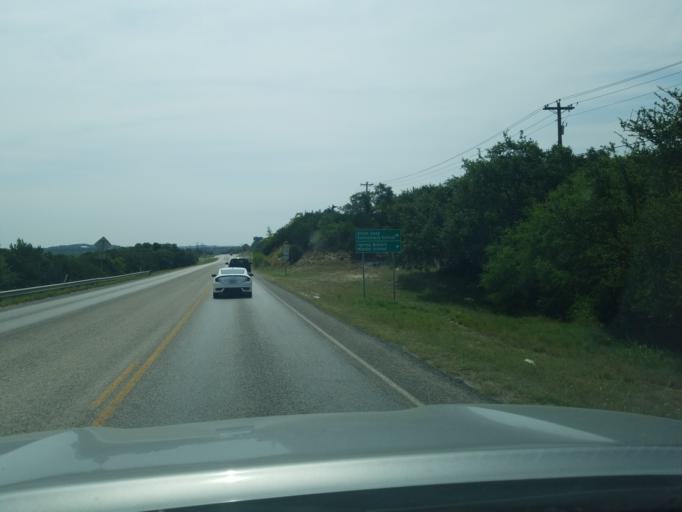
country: US
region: Texas
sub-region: Comal County
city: Bulverde
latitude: 29.7994
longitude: -98.4354
